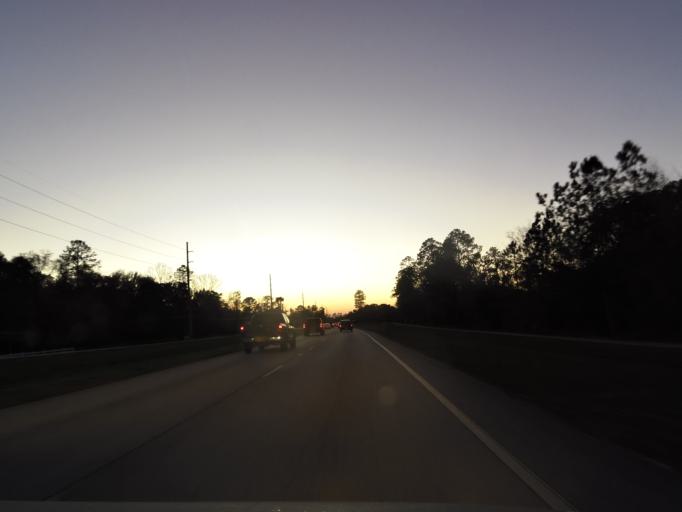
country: US
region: Florida
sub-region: Clay County
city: Lakeside
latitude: 30.1024
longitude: -81.7299
